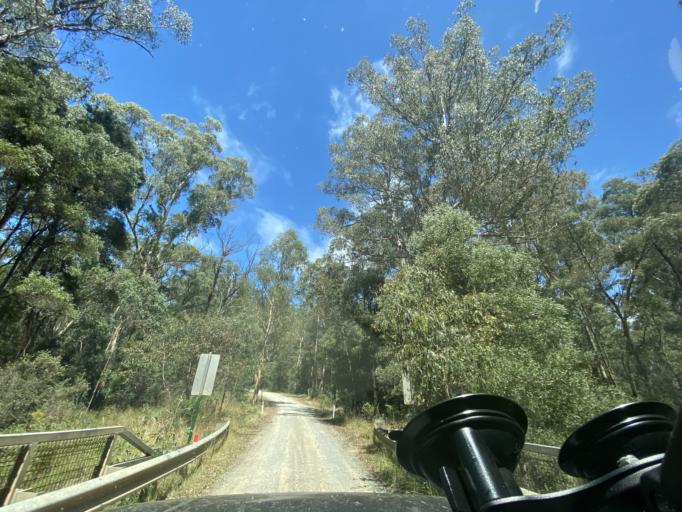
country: AU
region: Victoria
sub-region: Yarra Ranges
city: Millgrove
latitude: -37.5255
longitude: 146.0132
